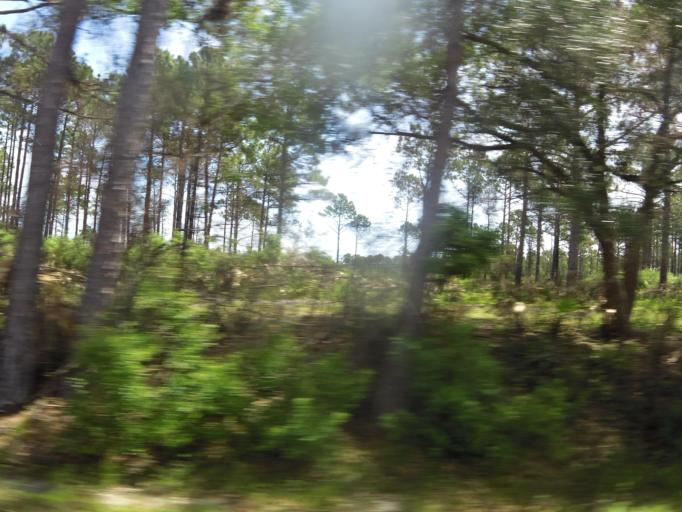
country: US
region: Florida
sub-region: Duval County
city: Atlantic Beach
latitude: 30.4737
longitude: -81.4865
